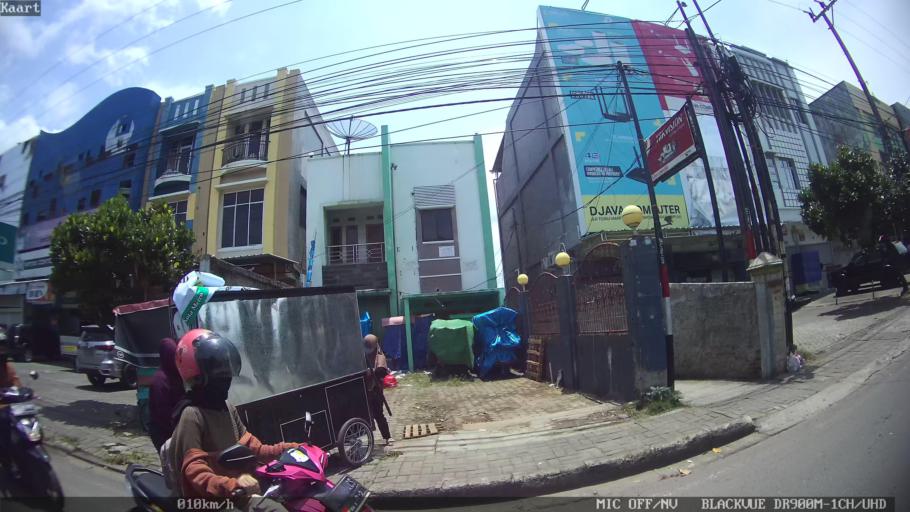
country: ID
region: Lampung
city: Kedaton
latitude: -5.3971
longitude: 105.2614
